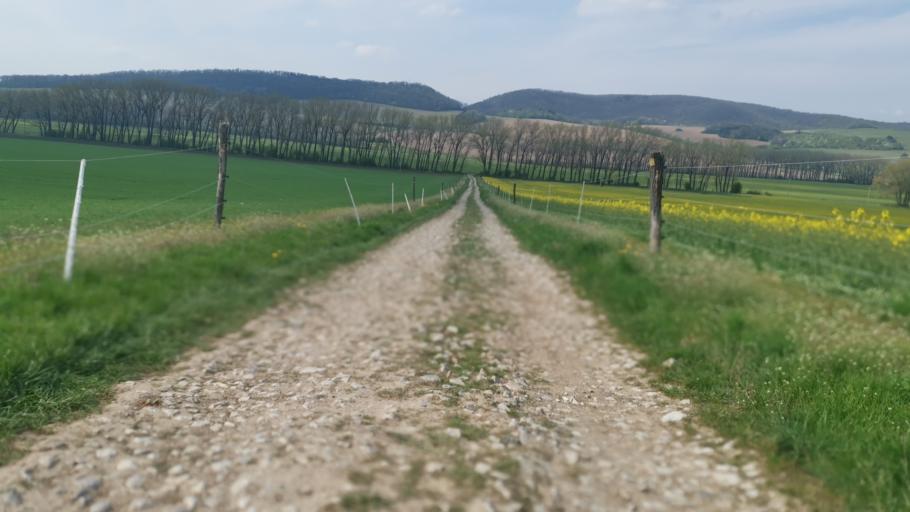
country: SK
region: Trnavsky
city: Smolenice
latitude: 48.5333
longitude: 17.3815
